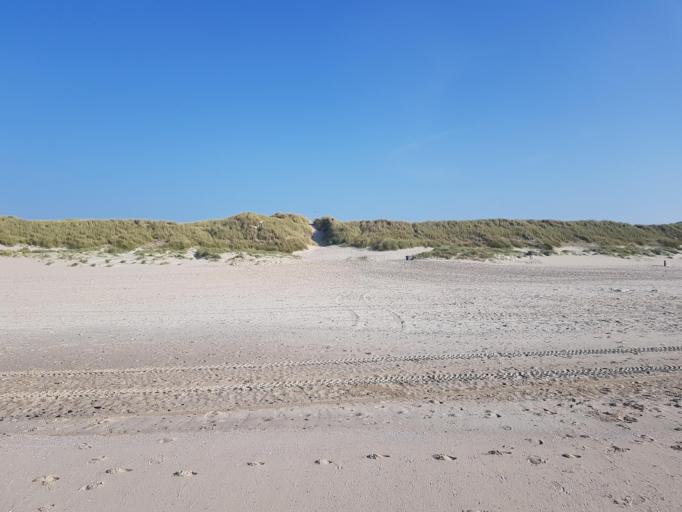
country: NL
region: North Holland
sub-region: Gemeente Texel
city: Den Burg
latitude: 53.1290
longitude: 4.7835
